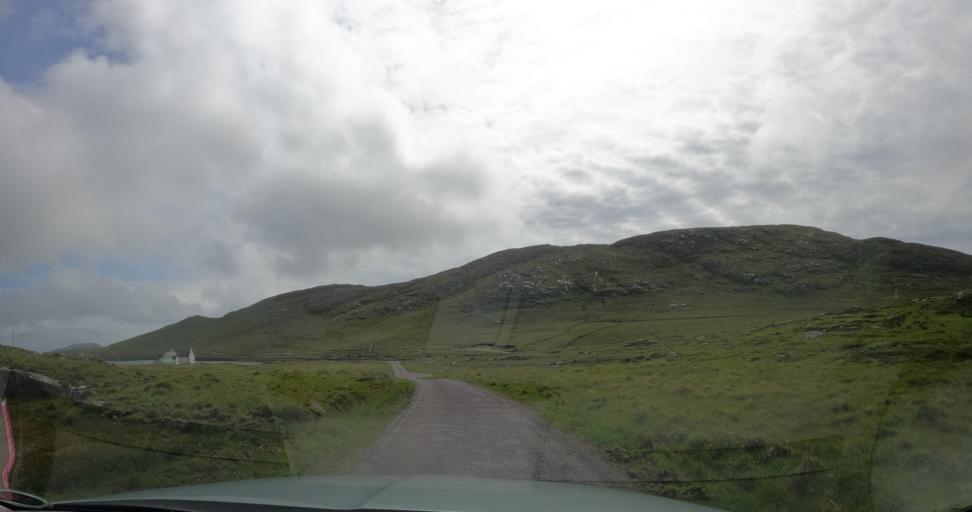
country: GB
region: Scotland
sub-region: Eilean Siar
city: Barra
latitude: 56.9416
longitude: -7.5431
